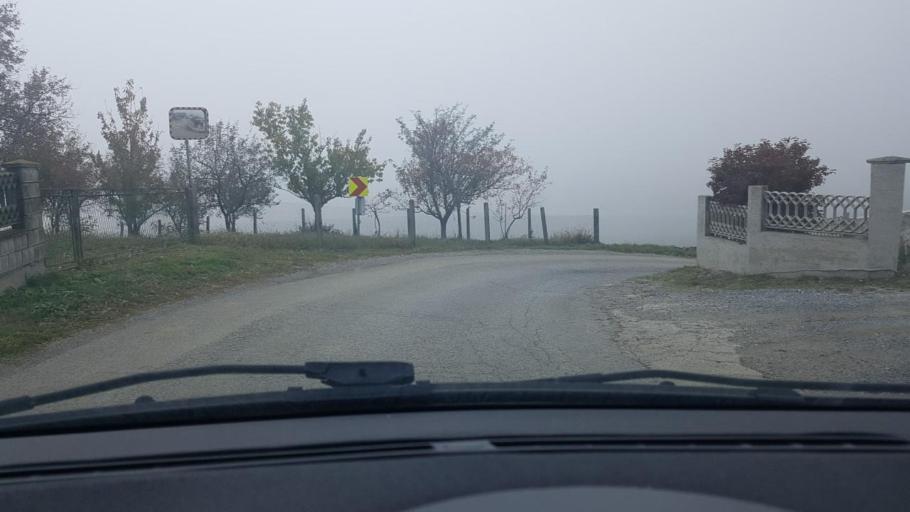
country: HR
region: Varazdinska
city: Lepoglava
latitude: 46.1530
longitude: 16.0313
